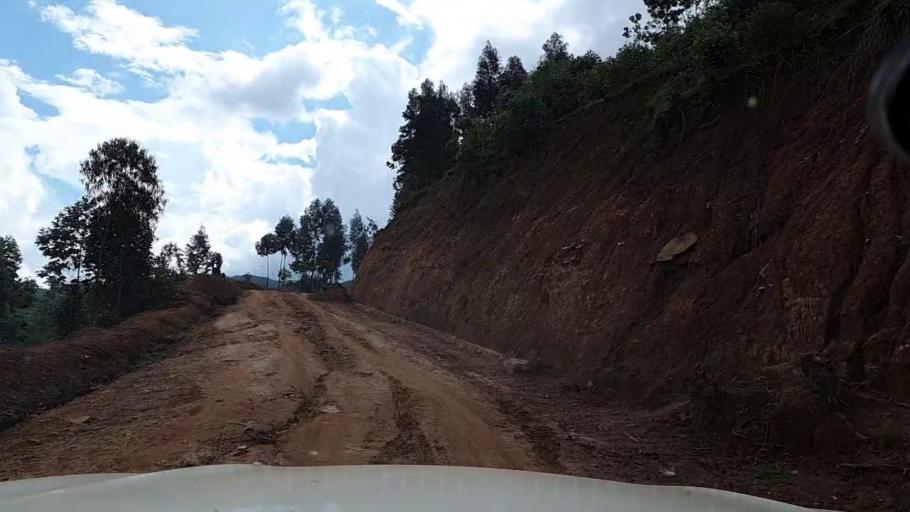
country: RW
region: Southern Province
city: Nzega
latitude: -2.7011
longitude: 29.4373
